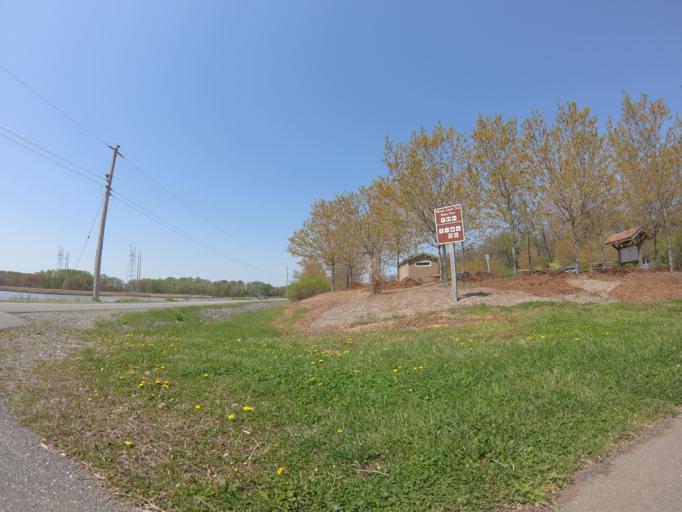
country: US
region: Delaware
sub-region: New Castle County
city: Delaware City
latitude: 39.5553
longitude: -75.6166
